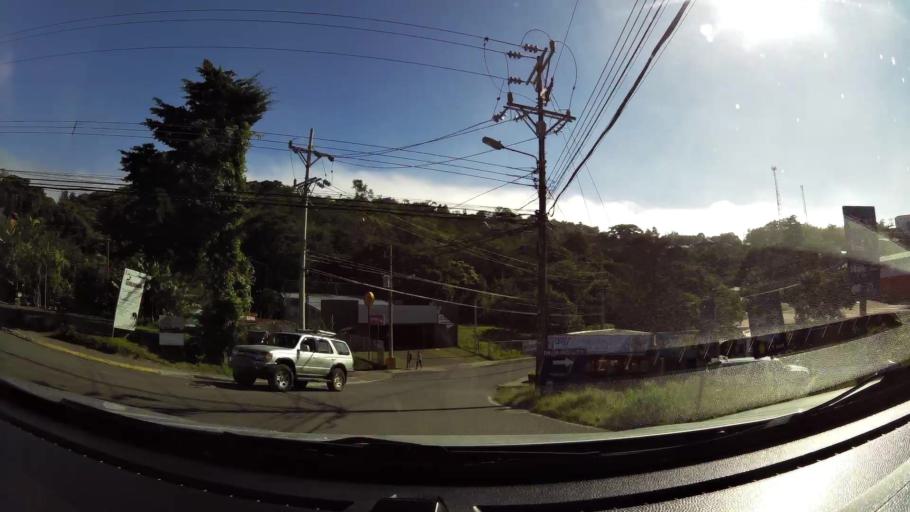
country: CR
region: Guanacaste
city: Juntas
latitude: 10.3169
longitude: -84.8234
